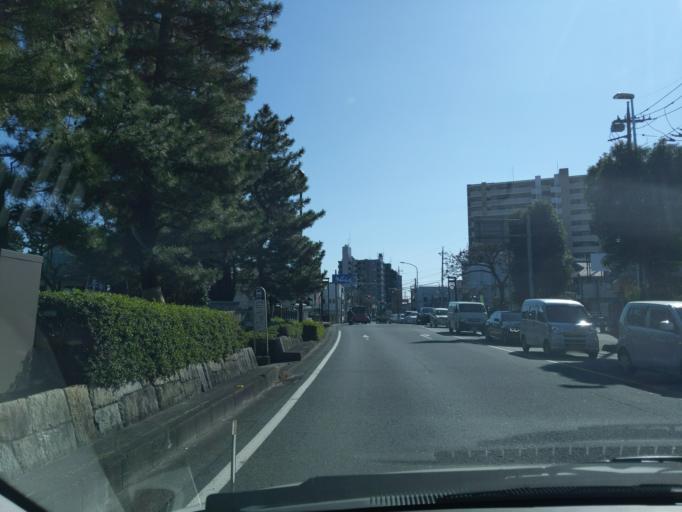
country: JP
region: Saitama
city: Soka
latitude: 35.8367
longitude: 139.8066
